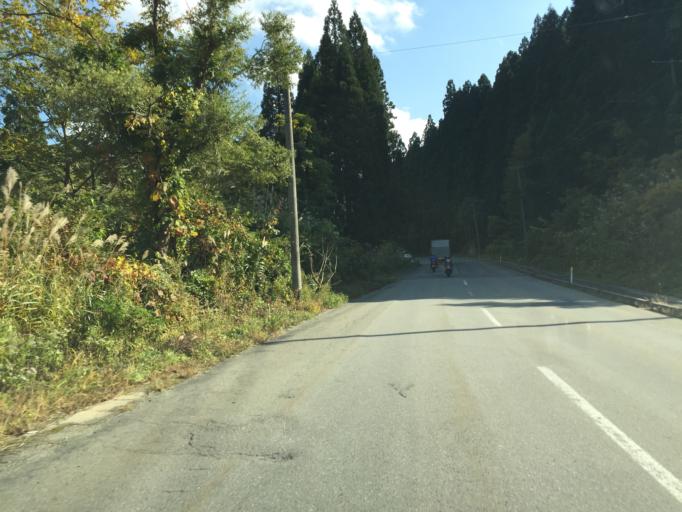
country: JP
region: Yamagata
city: Yonezawa
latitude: 37.8437
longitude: 139.9979
